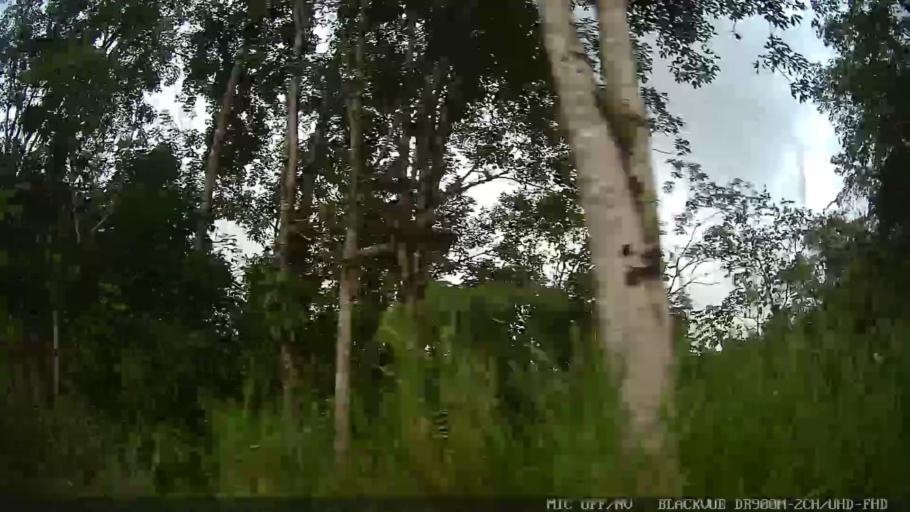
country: BR
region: Sao Paulo
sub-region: Itanhaem
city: Itanhaem
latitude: -24.0992
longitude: -46.8023
